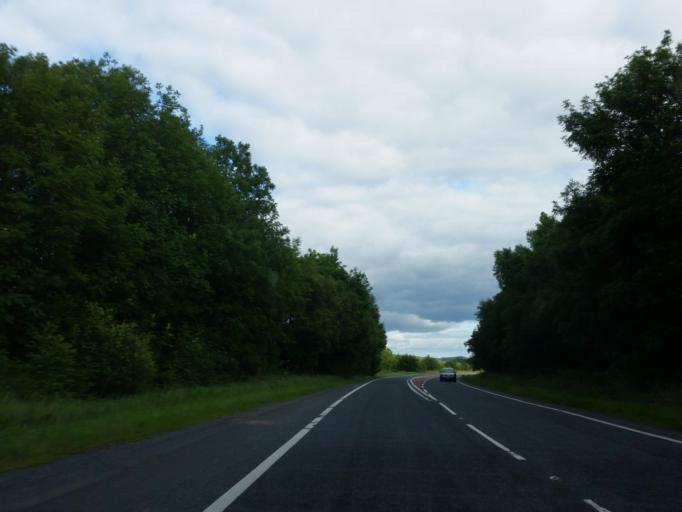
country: GB
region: Northern Ireland
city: Lisnaskea
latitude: 54.3106
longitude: -7.4962
